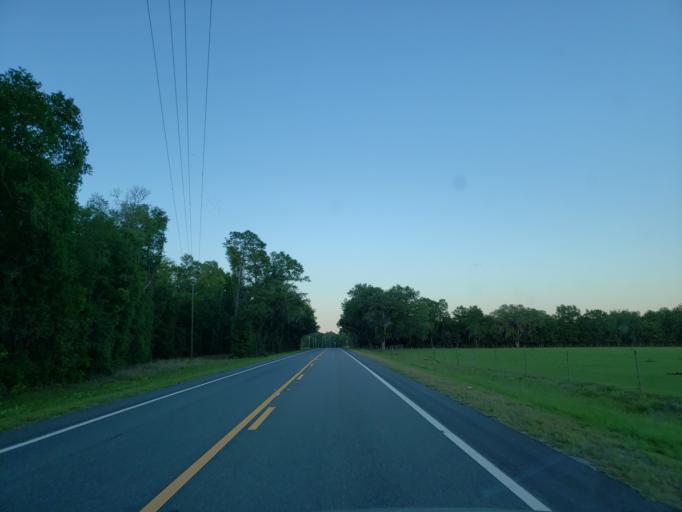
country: US
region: Georgia
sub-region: Echols County
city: Statenville
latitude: 30.5810
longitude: -83.1884
